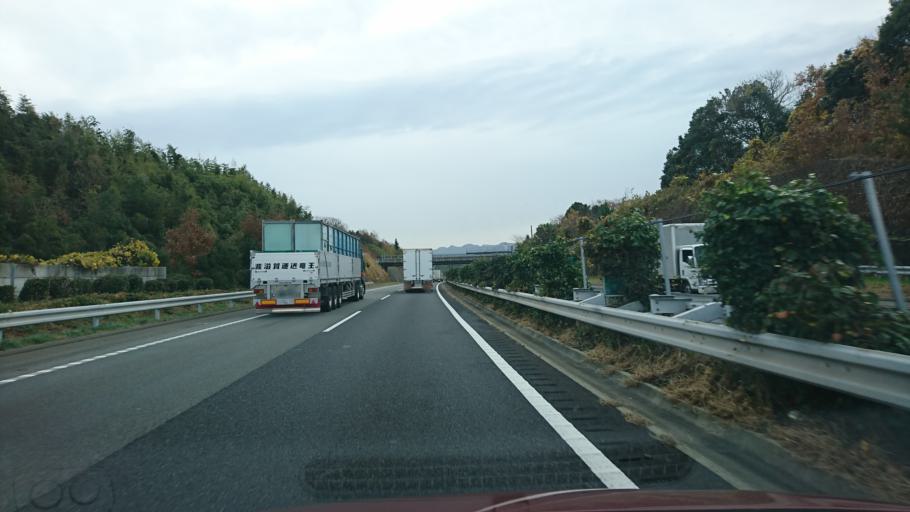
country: JP
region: Hyogo
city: Sandacho
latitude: 34.8302
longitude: 135.1676
